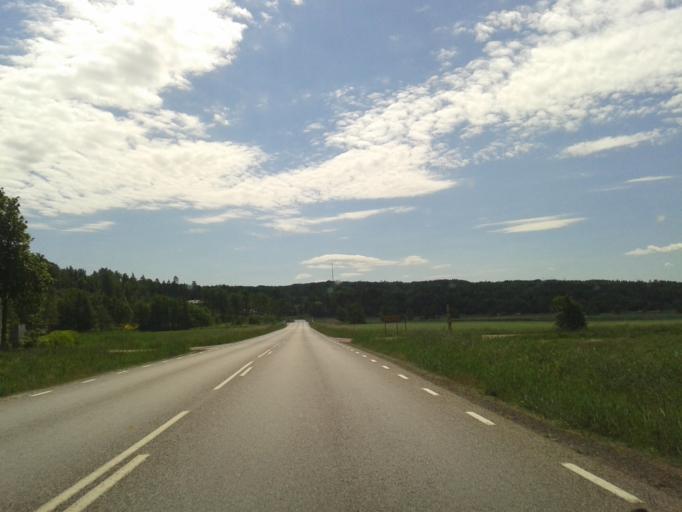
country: SE
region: Vaestra Goetaland
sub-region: Uddevalla Kommun
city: Ljungskile
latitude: 58.2829
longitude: 11.8906
